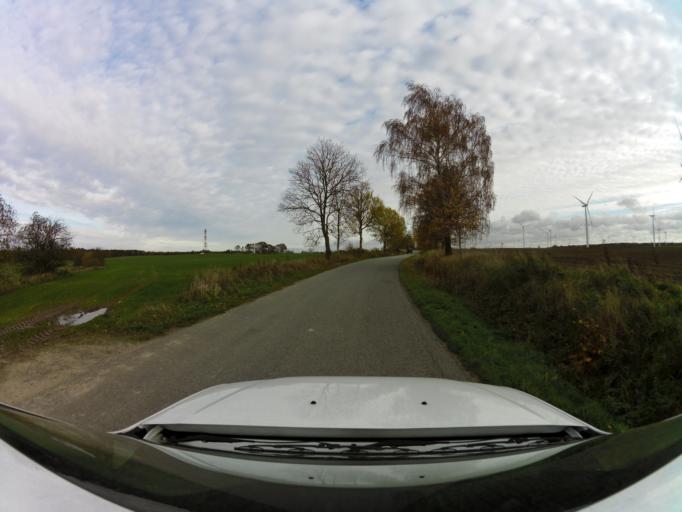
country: PL
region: West Pomeranian Voivodeship
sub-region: Powiat gryficki
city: Karnice
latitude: 54.0495
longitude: 15.0852
